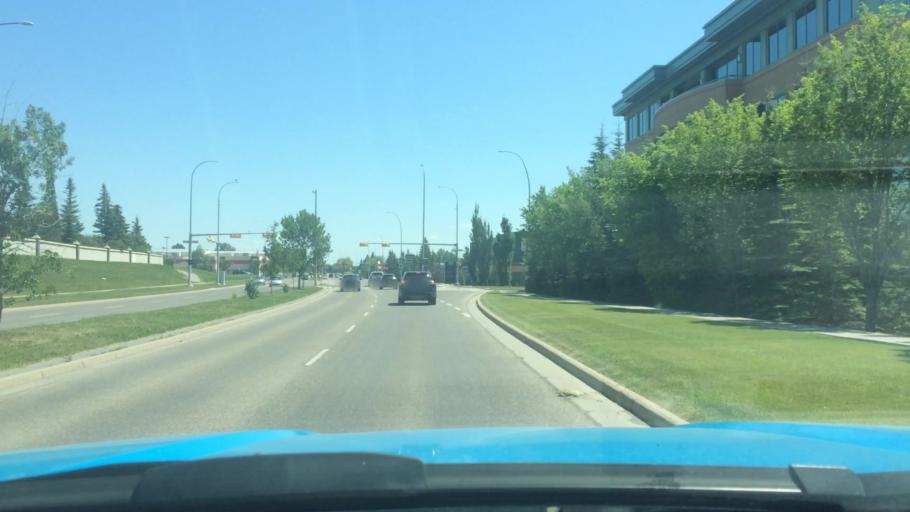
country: CA
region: Alberta
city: Calgary
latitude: 51.1305
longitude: -114.2011
